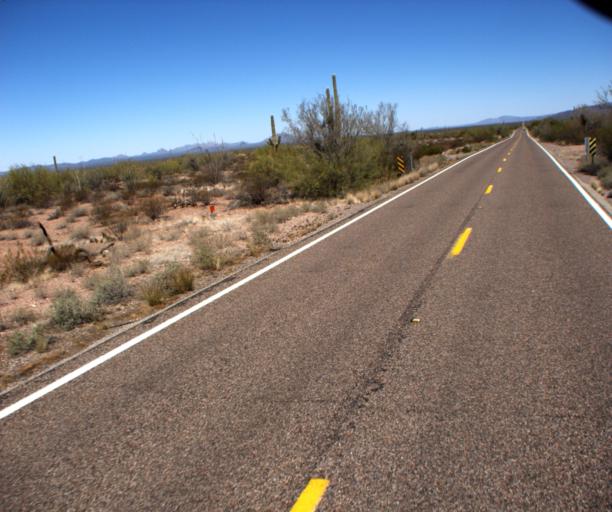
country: MX
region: Sonora
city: Sonoyta
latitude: 32.1085
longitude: -112.7702
